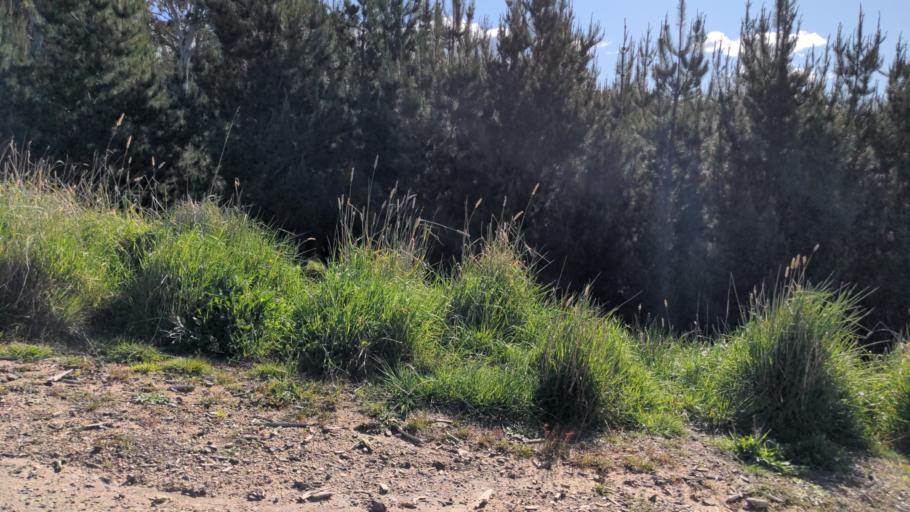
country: AU
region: New South Wales
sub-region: Blayney
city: Blayney
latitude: -33.4155
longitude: 149.3151
